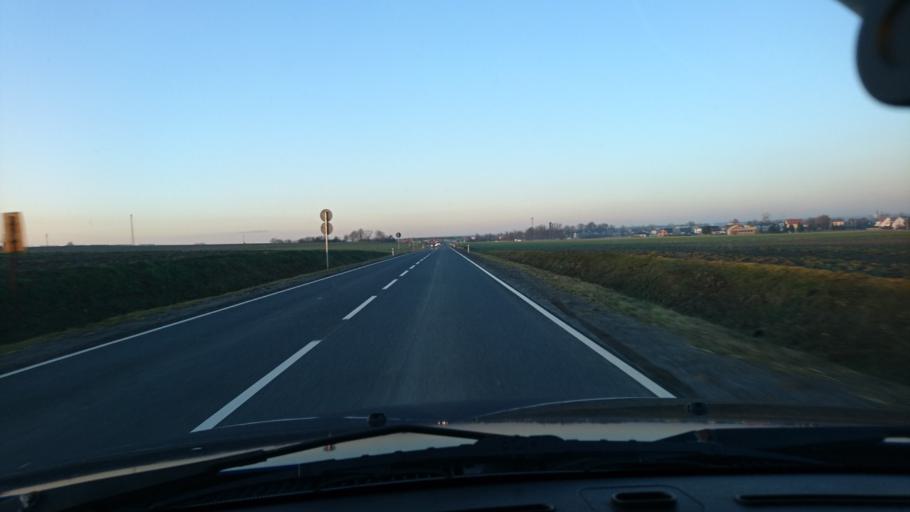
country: PL
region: Silesian Voivodeship
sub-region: Powiat gliwicki
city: Wielowies
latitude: 50.4971
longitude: 18.6066
